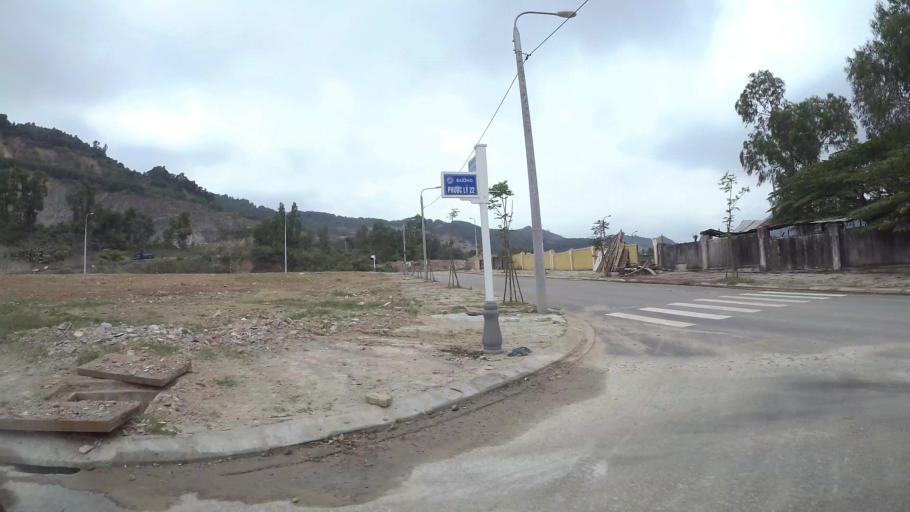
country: VN
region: Da Nang
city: Lien Chieu
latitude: 16.0433
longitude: 108.1630
